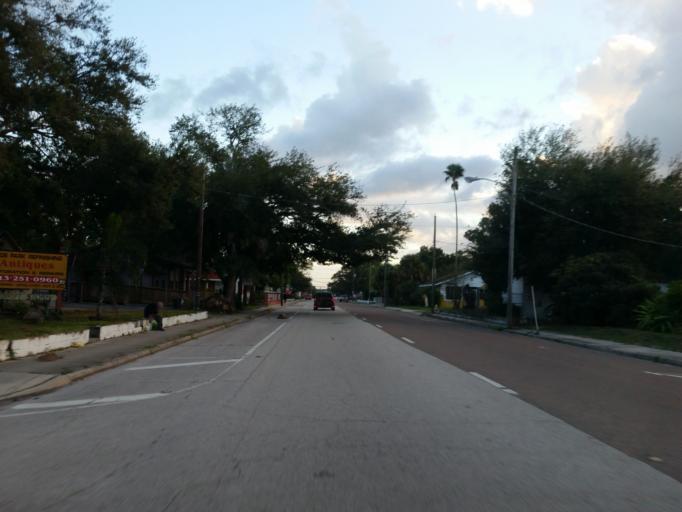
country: US
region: Florida
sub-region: Hillsborough County
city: Tampa
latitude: 27.9485
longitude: -82.4850
